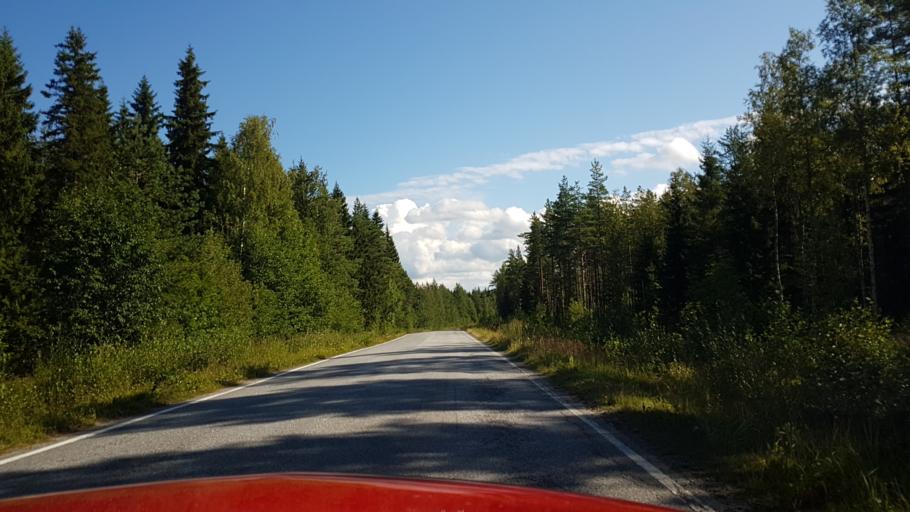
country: FI
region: Northern Ostrobothnia
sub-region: Ylivieska
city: Himanka
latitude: 64.0864
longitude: 23.7506
